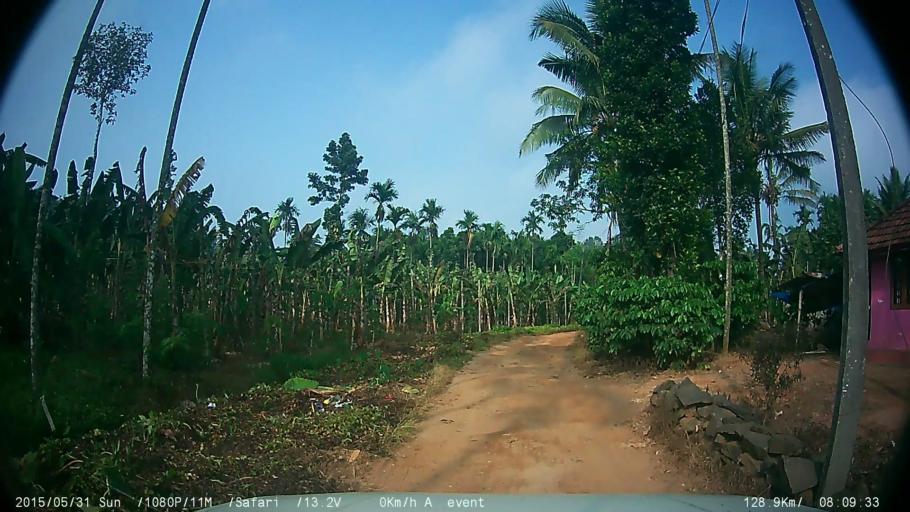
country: IN
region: Kerala
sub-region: Wayanad
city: Kalpetta
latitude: 11.6393
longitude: 76.0216
